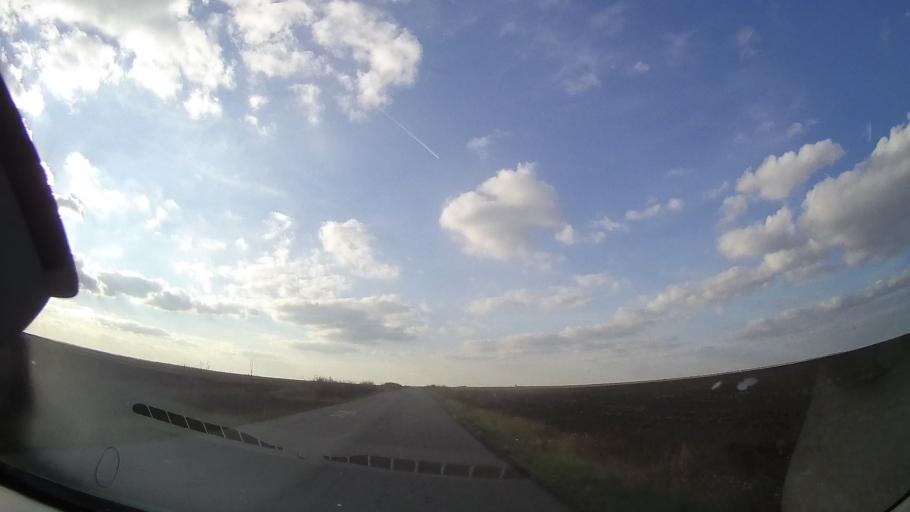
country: RO
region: Constanta
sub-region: Comuna Cerchezu
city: Cerchezu
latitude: 43.8240
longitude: 28.1422
